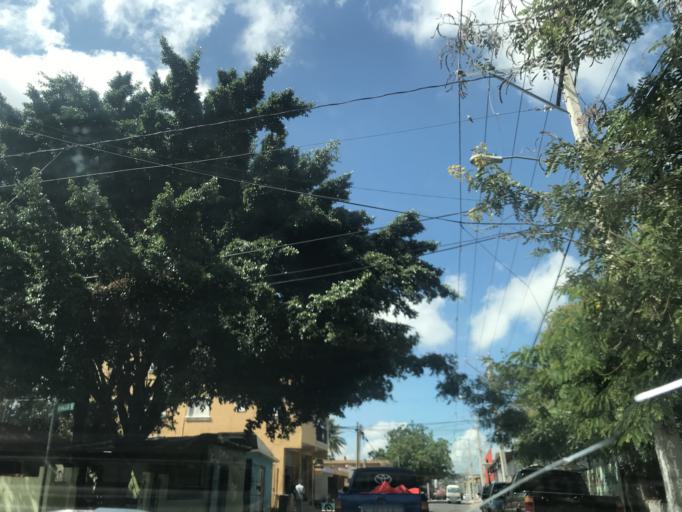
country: DO
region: Santiago
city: Palmar Arriba
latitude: 19.4917
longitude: -70.7412
